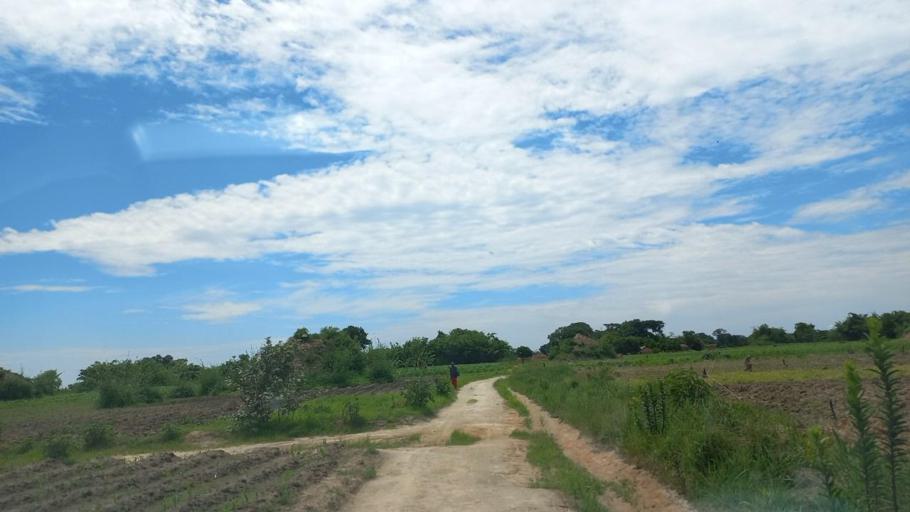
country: ZM
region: Copperbelt
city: Kitwe
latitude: -12.7977
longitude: 28.4012
